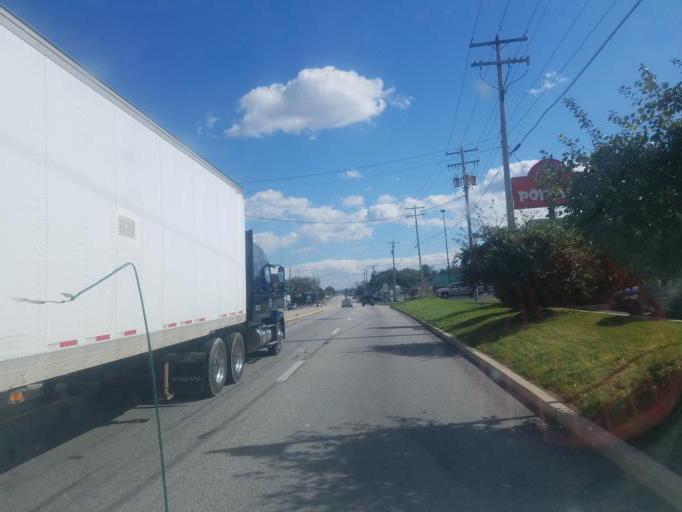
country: US
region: Pennsylvania
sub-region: Franklin County
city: Guilford
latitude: 39.9273
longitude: -77.6288
